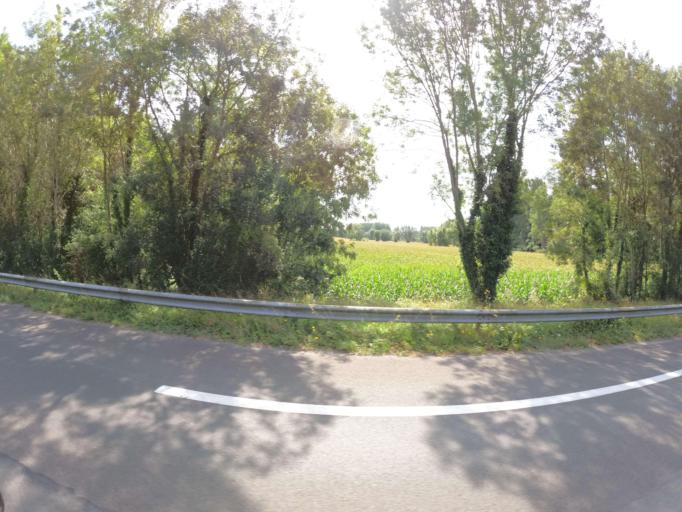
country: FR
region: Poitou-Charentes
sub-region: Departement des Deux-Sevres
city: Mauze-sur-le-Mignon
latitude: 46.1897
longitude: -0.6687
